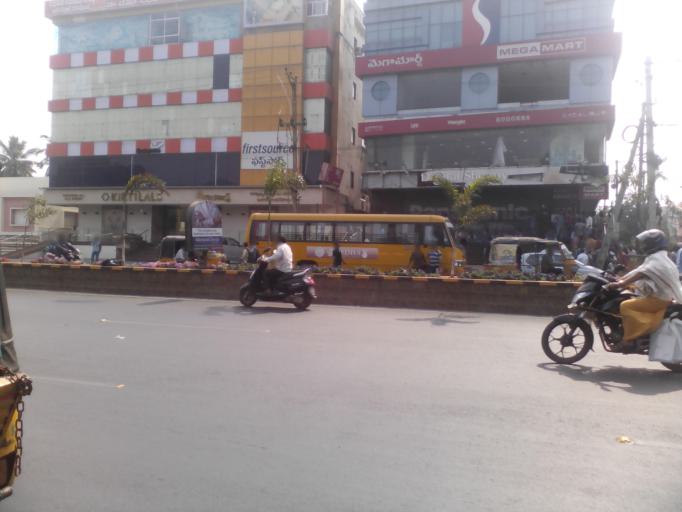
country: IN
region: Andhra Pradesh
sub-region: Krishna
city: Vijayawada
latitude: 16.5060
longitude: 80.6369
